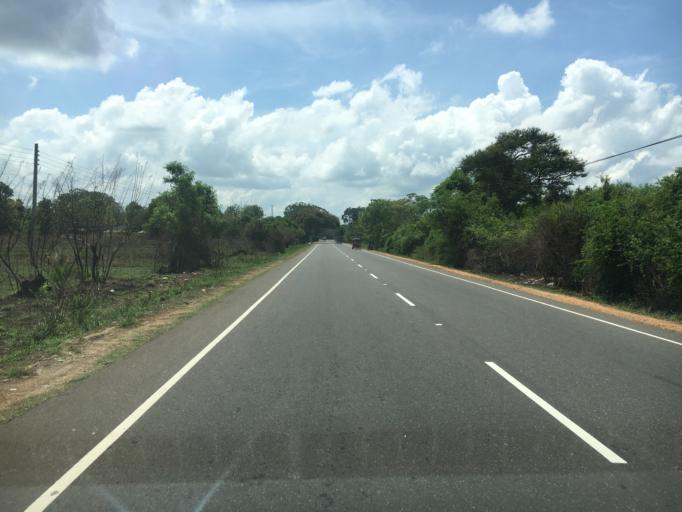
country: LK
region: North Central
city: Anuradhapura
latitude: 8.2777
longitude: 80.4974
